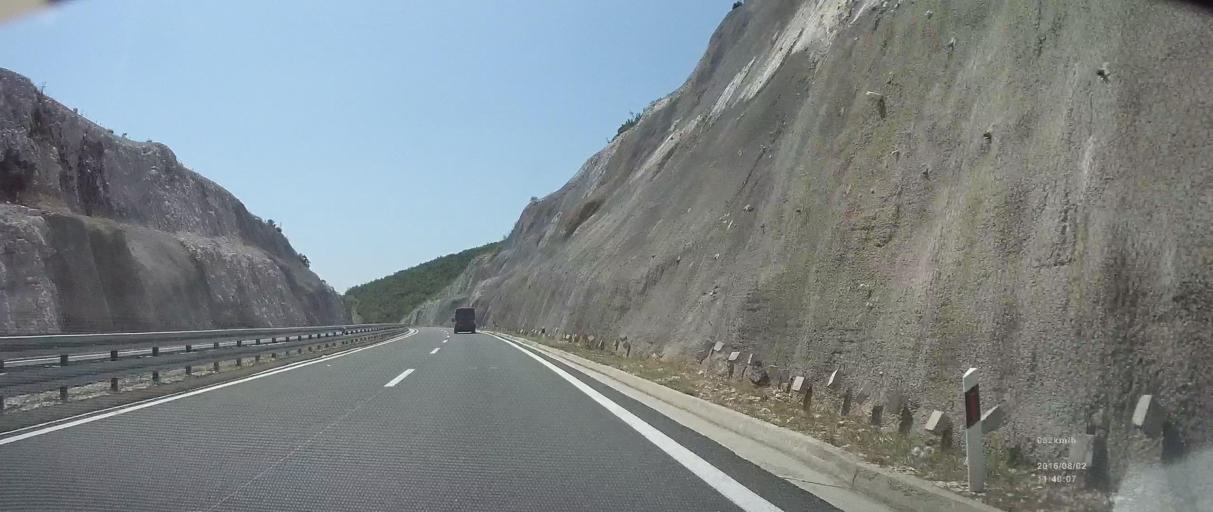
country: HR
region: Dubrovacko-Neretvanska
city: Komin
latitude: 43.0784
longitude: 17.4896
